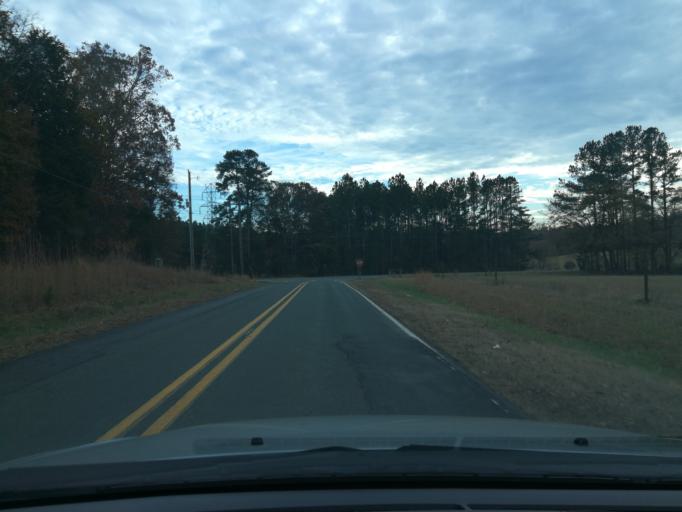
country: US
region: North Carolina
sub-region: Orange County
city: Chapel Hill
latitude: 36.0013
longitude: -79.0466
